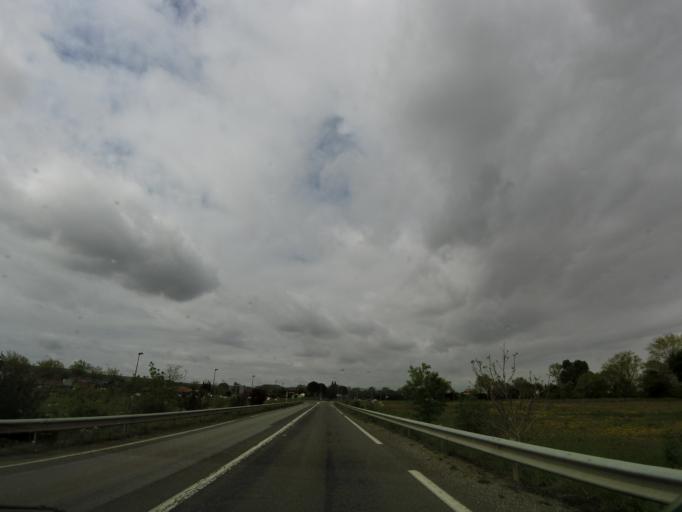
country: FR
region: Languedoc-Roussillon
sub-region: Departement de l'Aude
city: Castelnaudary
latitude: 43.3015
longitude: 1.9587
